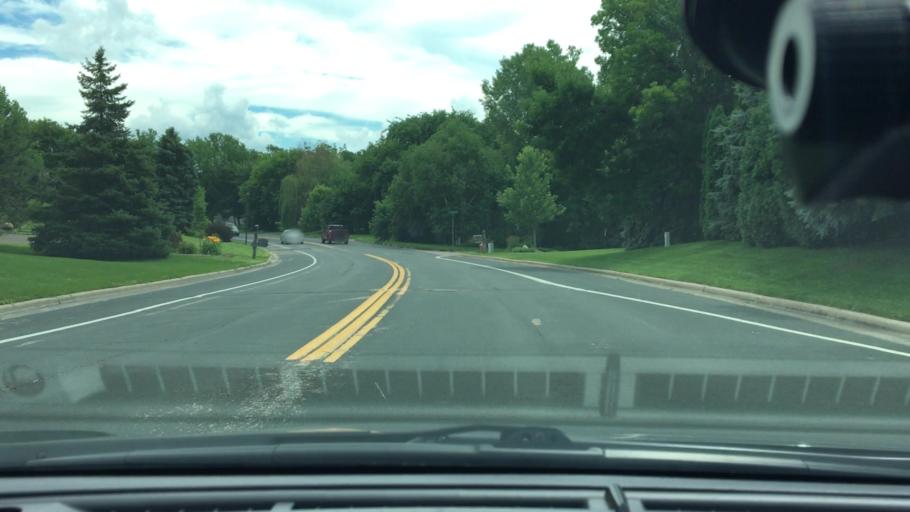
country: US
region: Minnesota
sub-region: Hennepin County
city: New Hope
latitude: 45.0097
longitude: -93.4111
